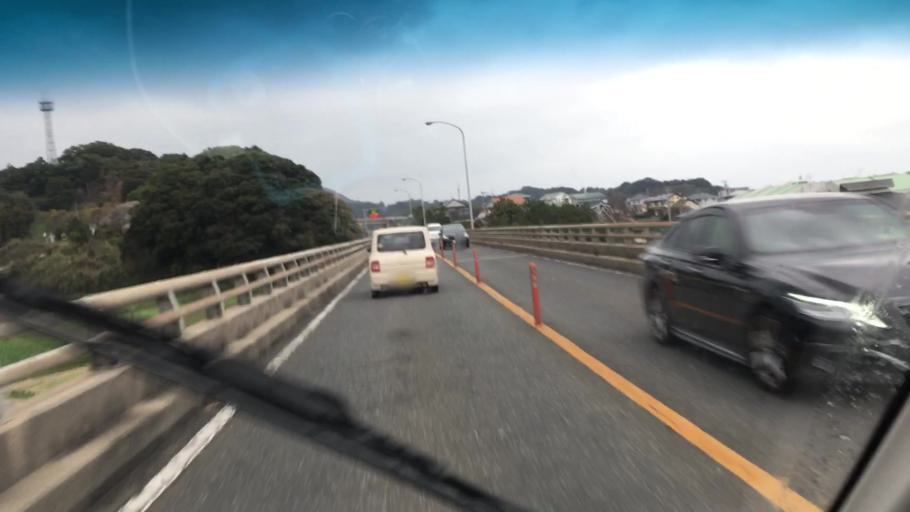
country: JP
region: Fukuoka
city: Maebaru-chuo
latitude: 33.5014
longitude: 130.0879
